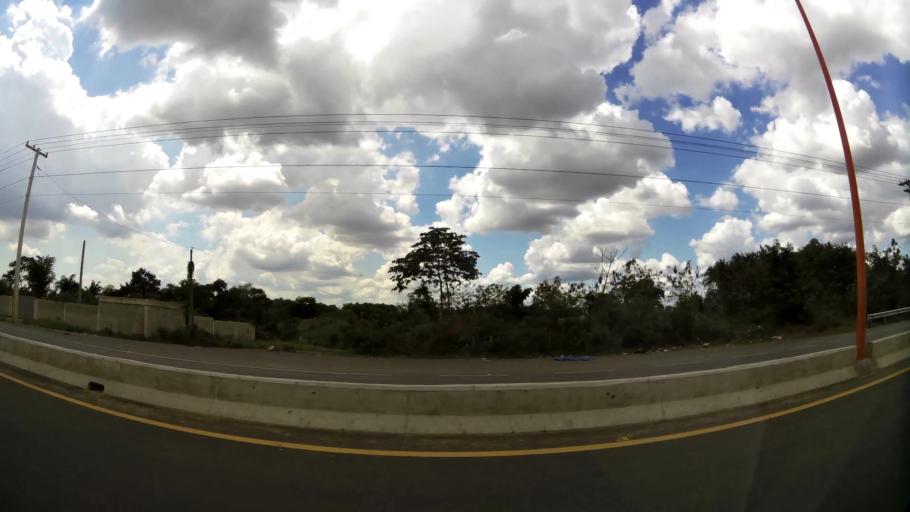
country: DO
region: Nacional
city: Santo Domingo
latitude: 18.5594
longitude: -69.9775
